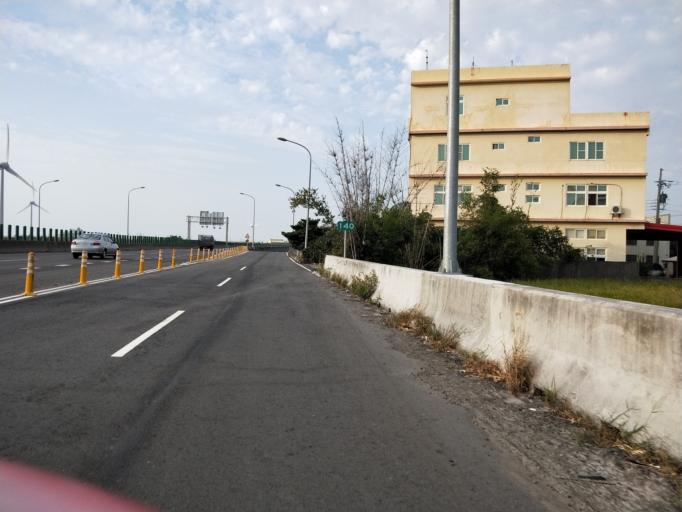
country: TW
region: Taiwan
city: Fengyuan
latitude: 24.3664
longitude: 120.5858
